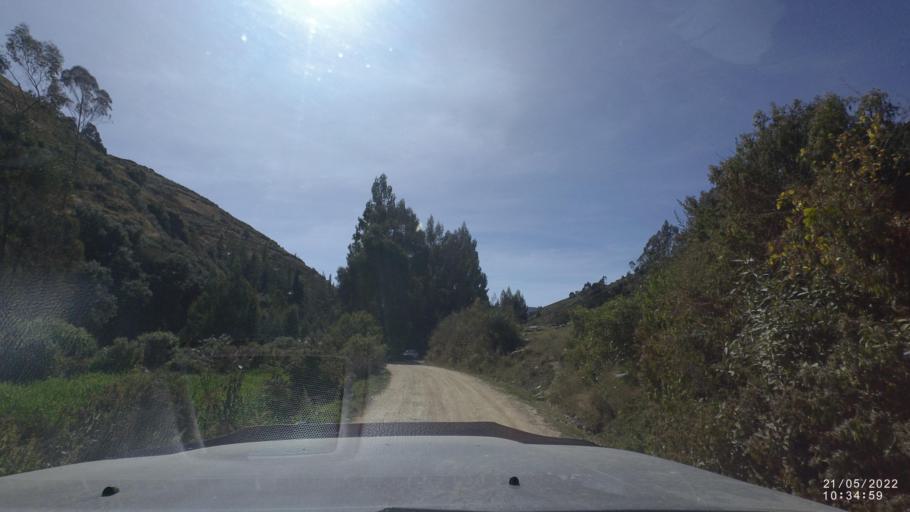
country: BO
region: Cochabamba
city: Colomi
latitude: -17.3190
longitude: -65.9297
